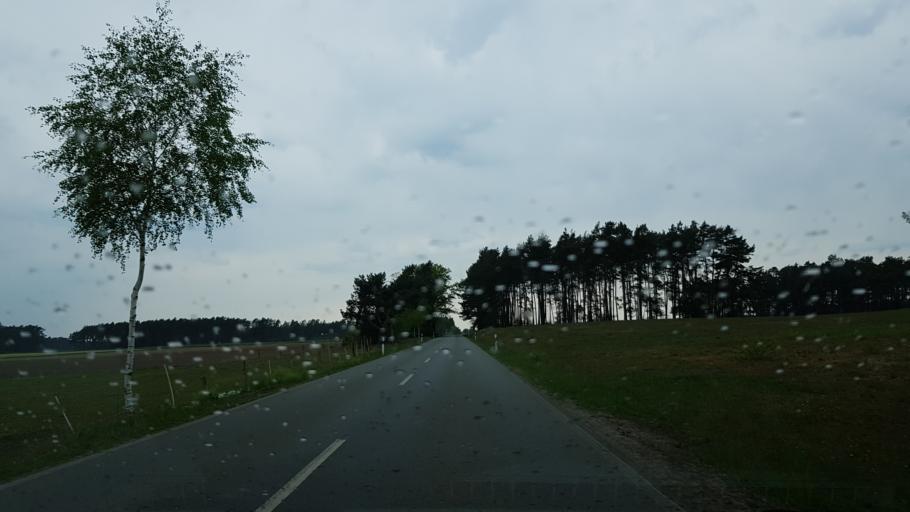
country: DE
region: Lower Saxony
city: Gartow
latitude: 53.0582
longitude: 11.4252
